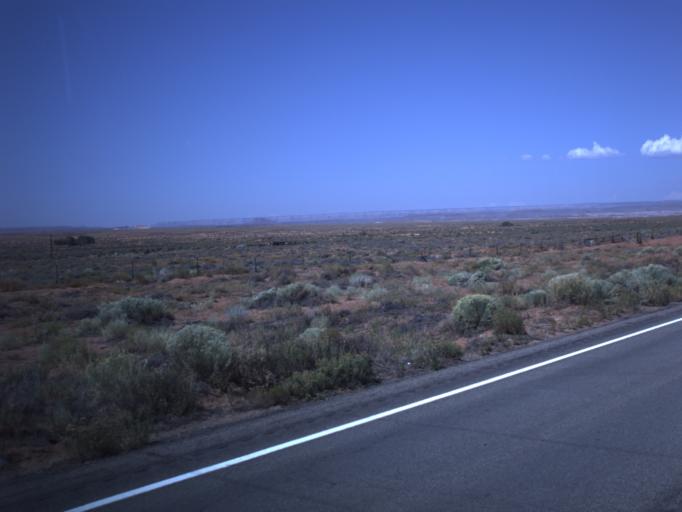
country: US
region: Utah
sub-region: San Juan County
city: Blanding
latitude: 37.1556
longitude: -109.5696
